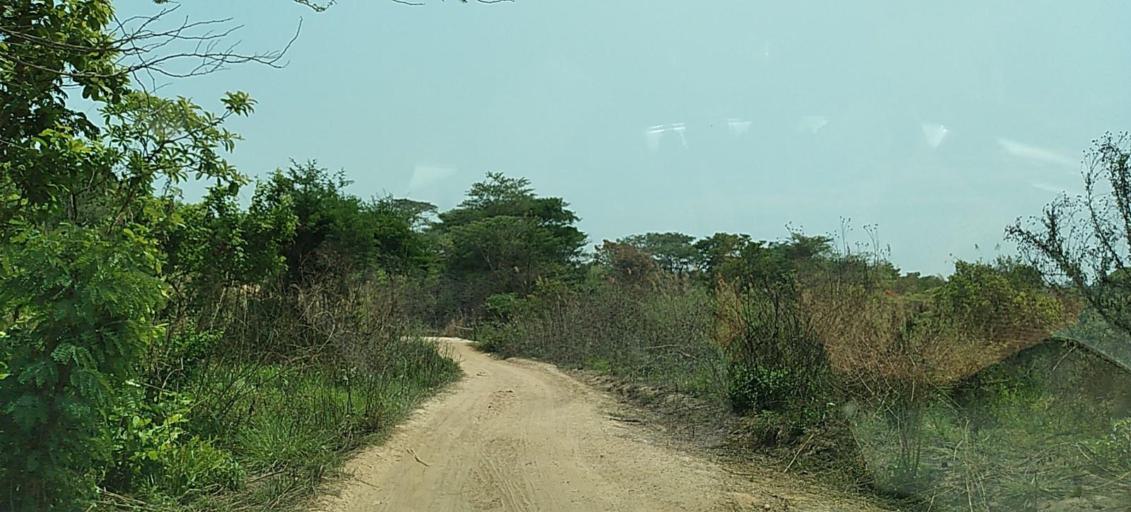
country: ZM
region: Copperbelt
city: Kalulushi
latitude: -12.9556
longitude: 28.1492
